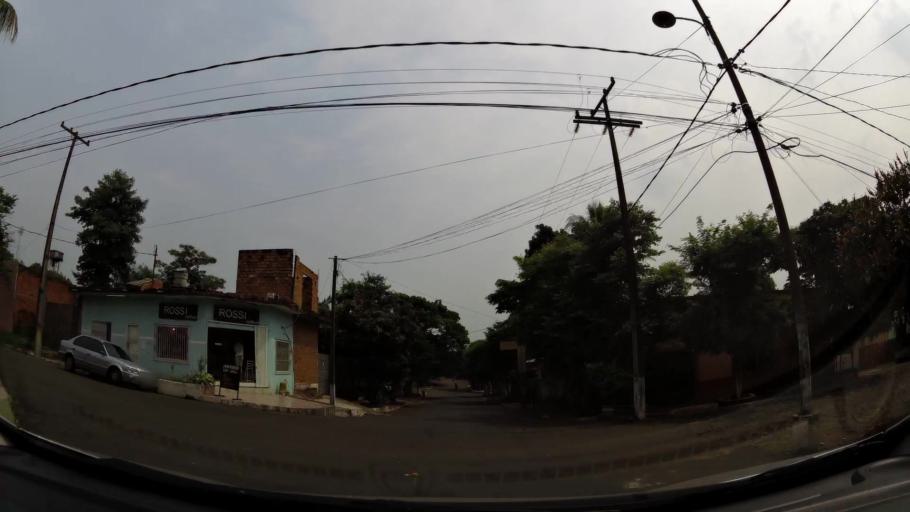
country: BR
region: Parana
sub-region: Foz Do Iguacu
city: Foz do Iguacu
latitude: -25.5554
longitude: -54.6047
